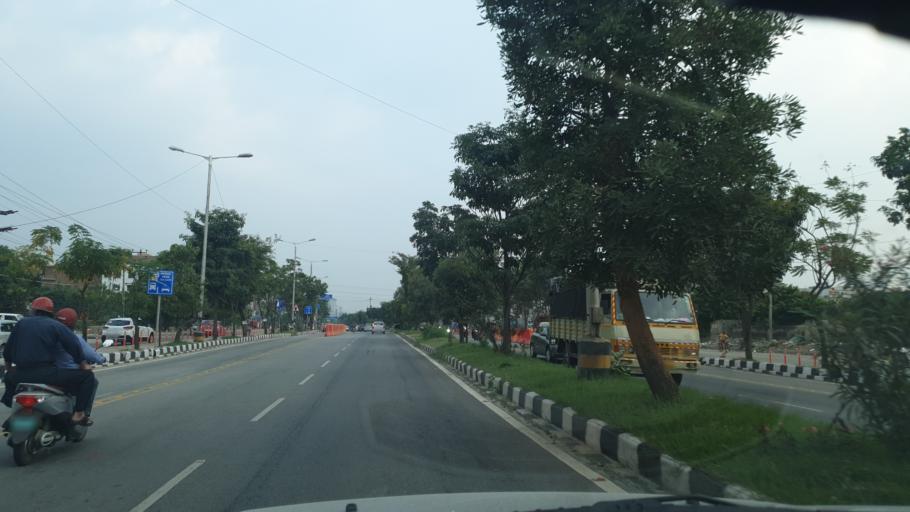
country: IN
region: Karnataka
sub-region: Bangalore Urban
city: Bangalore
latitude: 12.9972
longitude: 77.6831
